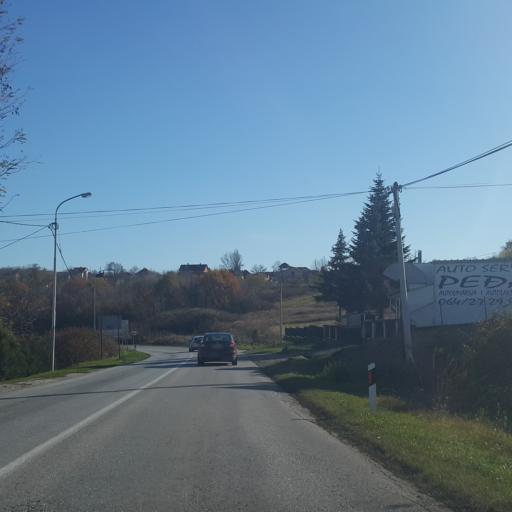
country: RS
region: Central Serbia
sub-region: Sumadijski Okrug
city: Topola
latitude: 44.2650
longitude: 20.6901
